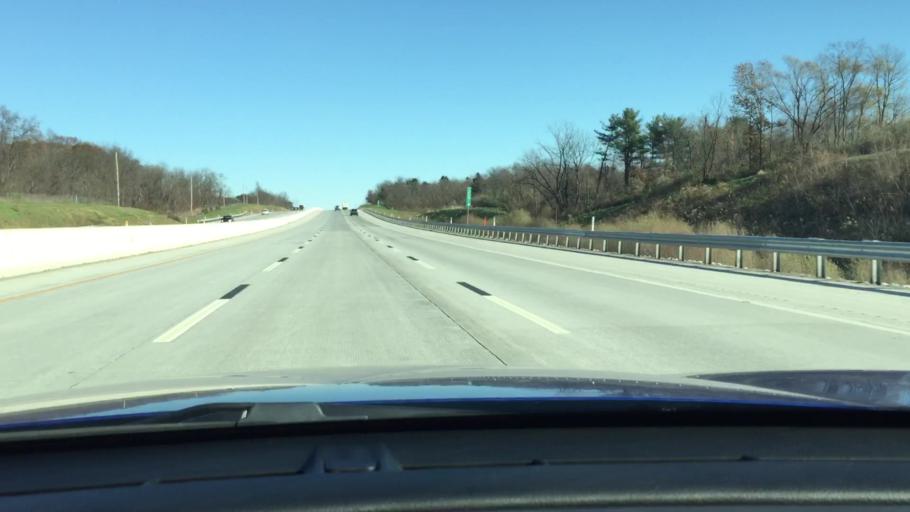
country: US
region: Pennsylvania
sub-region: Cumberland County
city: Newville
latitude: 40.1805
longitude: -77.5028
